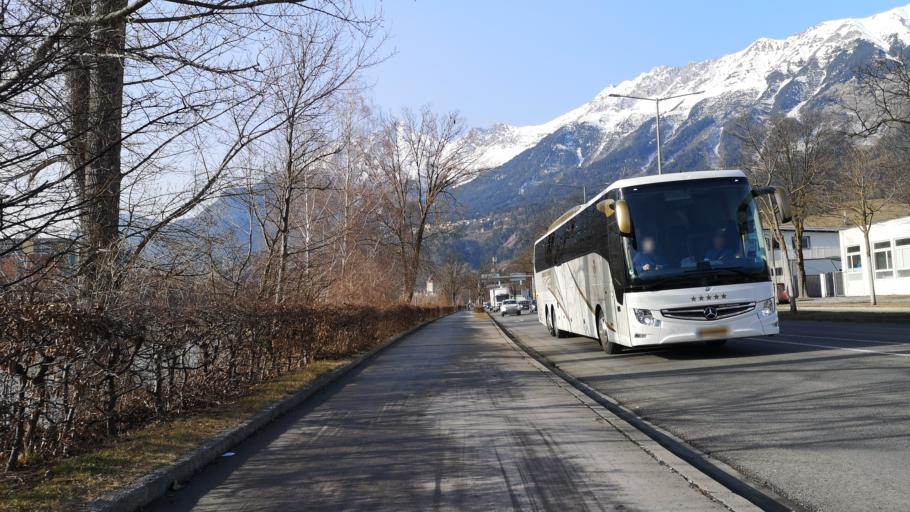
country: AT
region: Tyrol
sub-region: Politischer Bezirk Innsbruck Land
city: Rum
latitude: 47.2758
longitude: 11.4281
